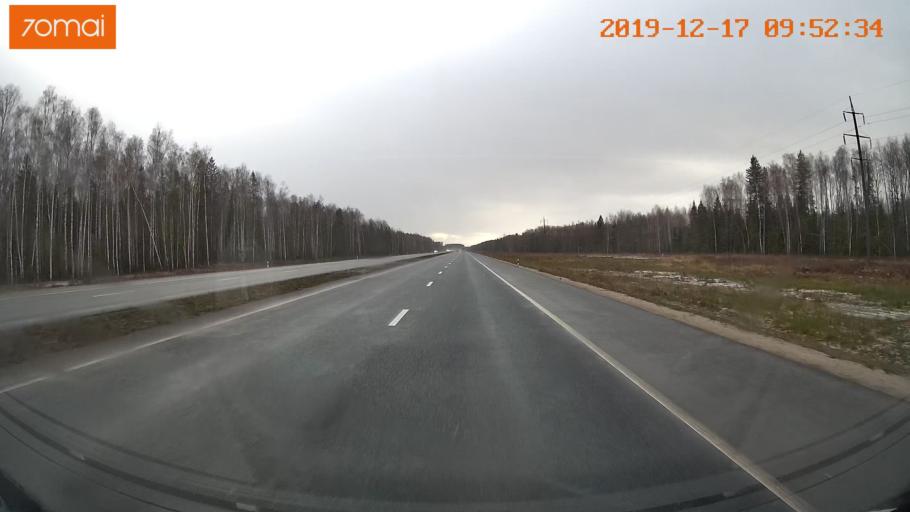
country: RU
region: Vladimir
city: Kommunar
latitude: 56.0314
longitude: 40.5415
